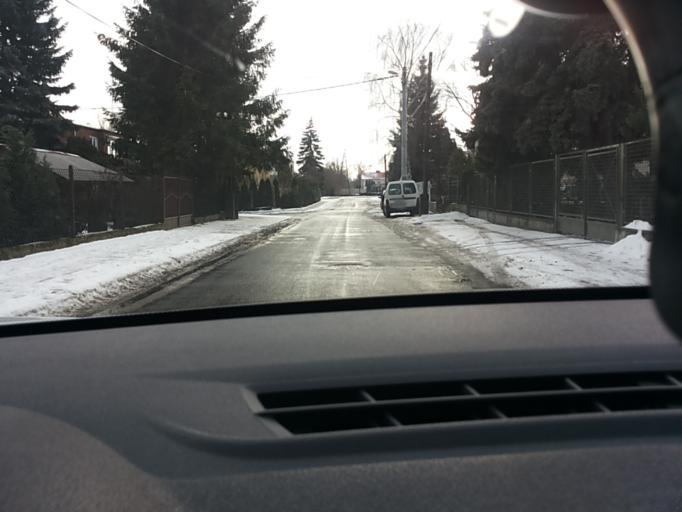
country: PL
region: Lodz Voivodeship
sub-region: Skierniewice
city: Skierniewice
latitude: 51.9600
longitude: 20.1359
